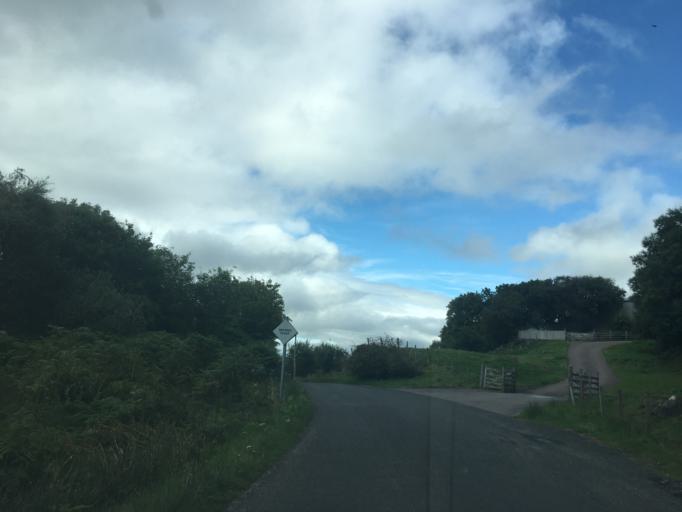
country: GB
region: Scotland
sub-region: Argyll and Bute
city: Ardrishaig
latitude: 56.0882
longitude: -5.5603
